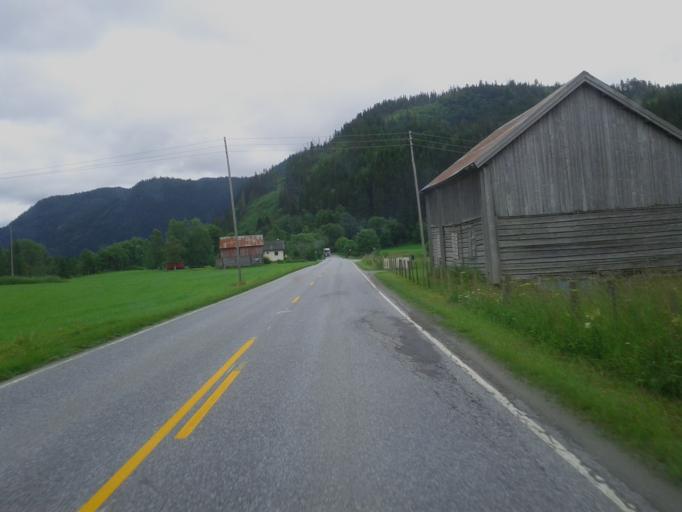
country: NO
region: Sor-Trondelag
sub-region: Midtre Gauldal
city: Storen
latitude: 63.0186
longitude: 10.3329
